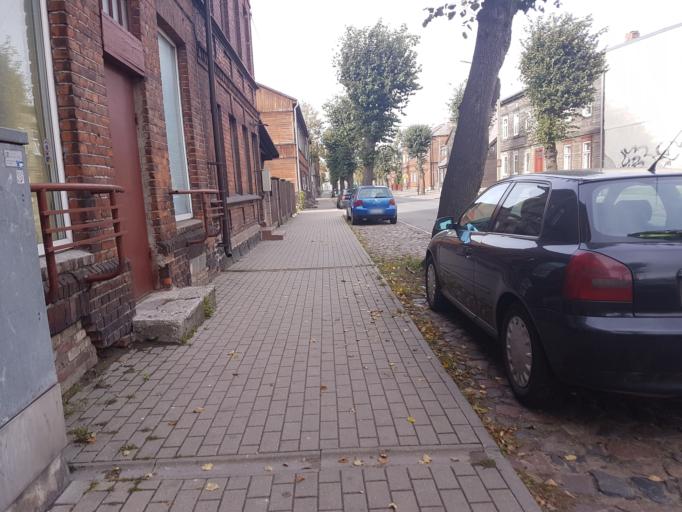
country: LV
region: Liepaja
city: Liepaja
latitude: 56.5192
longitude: 21.0124
